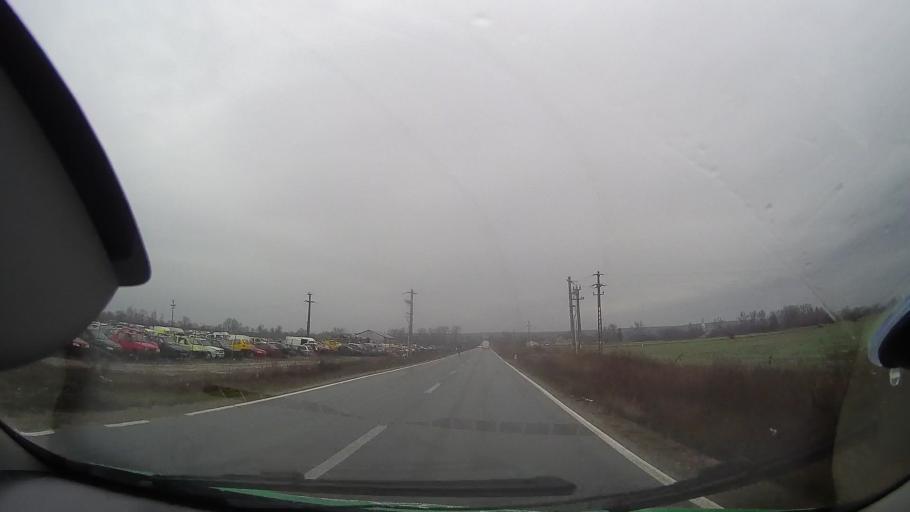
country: RO
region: Bihor
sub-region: Comuna Tinca
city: Tinca
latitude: 46.7630
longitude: 21.9343
